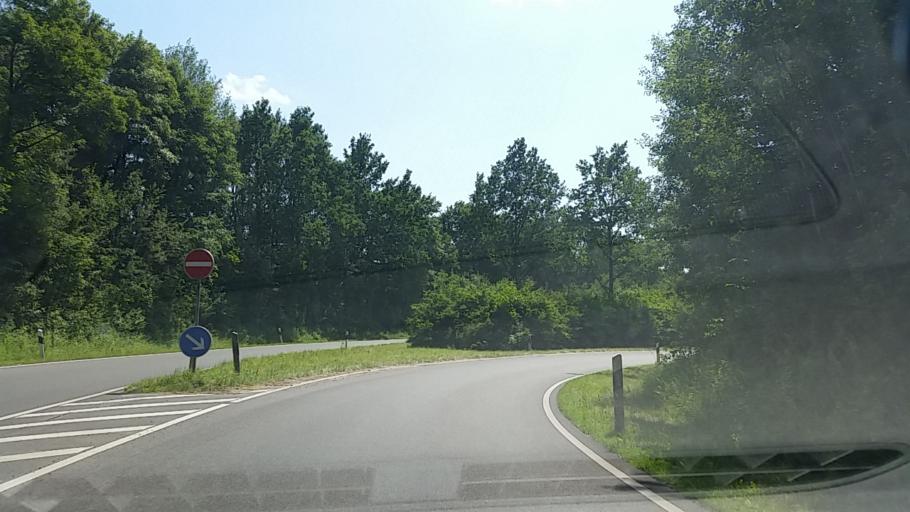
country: DE
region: Schleswig-Holstein
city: Reinbek
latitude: 53.5475
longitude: 10.2388
